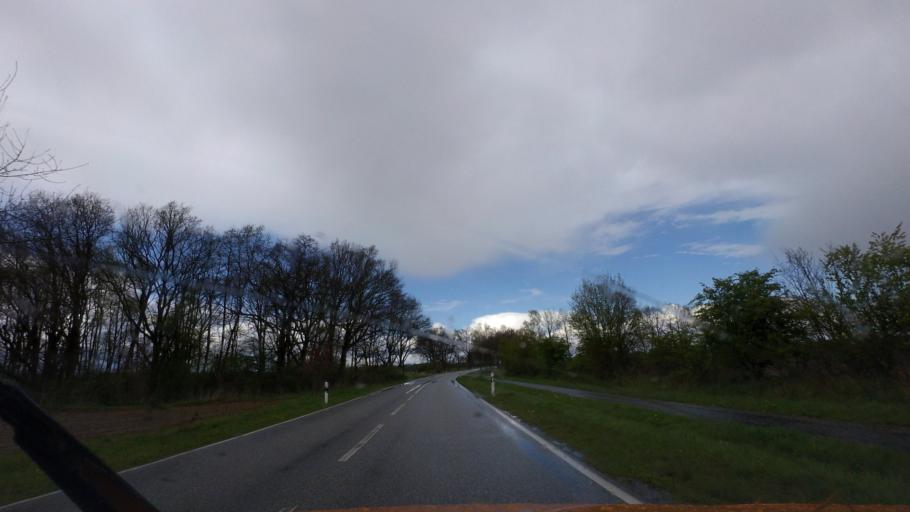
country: DE
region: Schleswig-Holstein
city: Lanze
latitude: 53.3831
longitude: 10.6279
